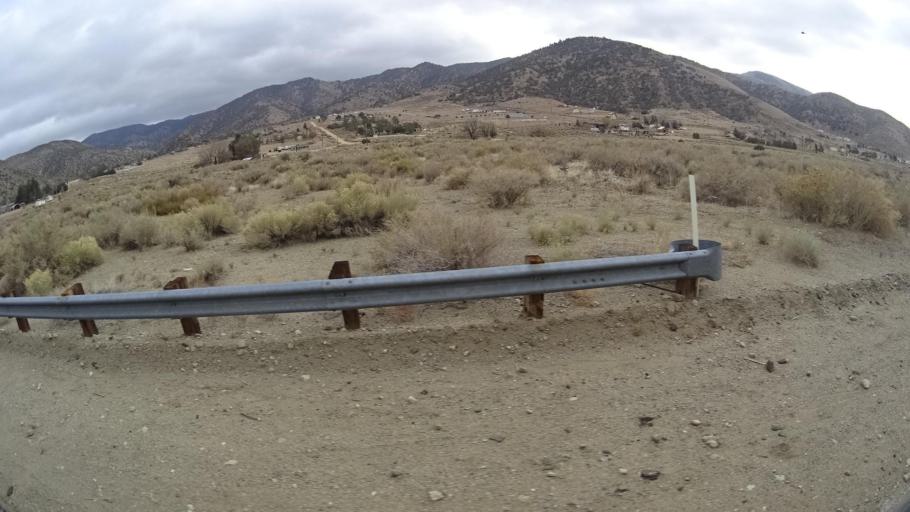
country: US
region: California
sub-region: Kern County
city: Tehachapi
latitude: 35.1466
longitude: -118.3113
